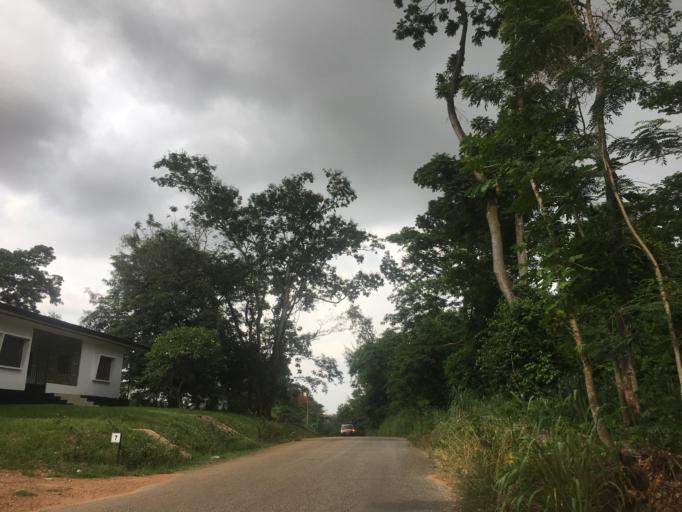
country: GH
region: Ashanti
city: Mamponteng
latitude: 6.6855
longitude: -1.5661
